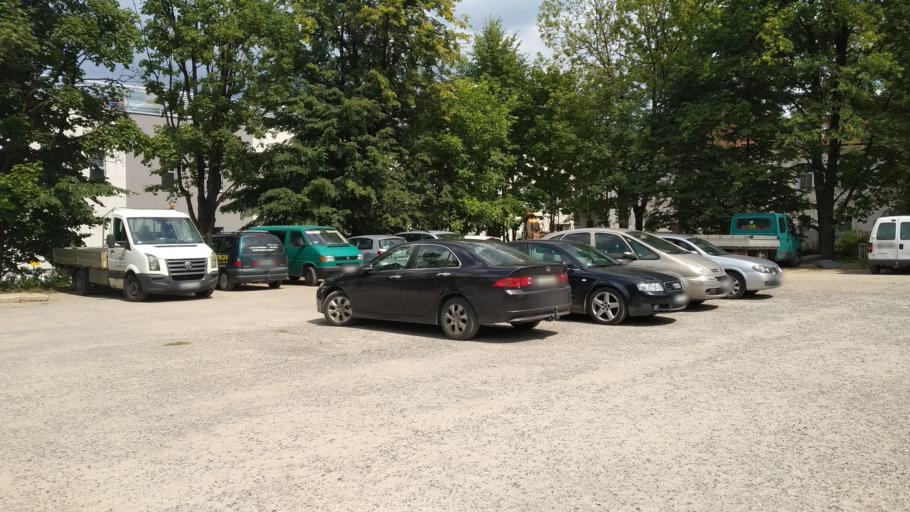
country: PL
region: Lesser Poland Voivodeship
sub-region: Powiat krakowski
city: Rzaska
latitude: 50.0630
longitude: 19.8671
